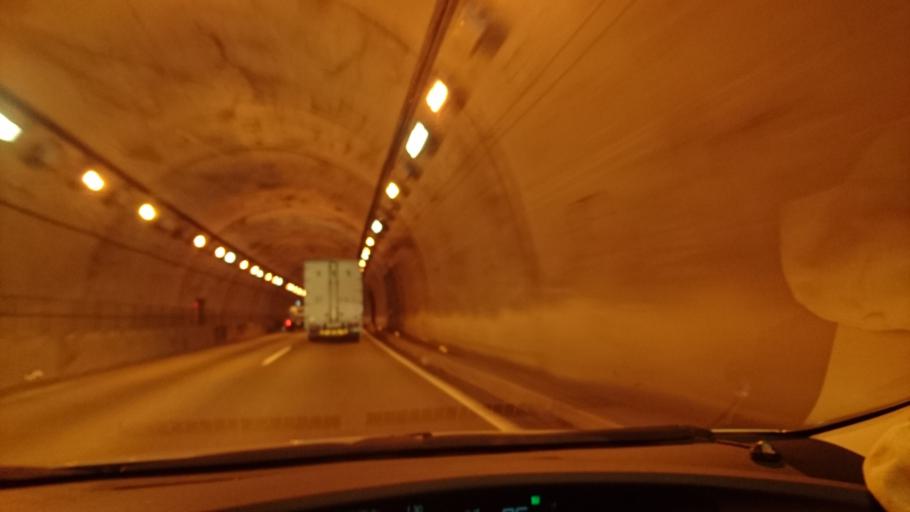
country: JP
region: Shiga Prefecture
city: Otsu-shi
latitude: 34.9480
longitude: 135.8925
